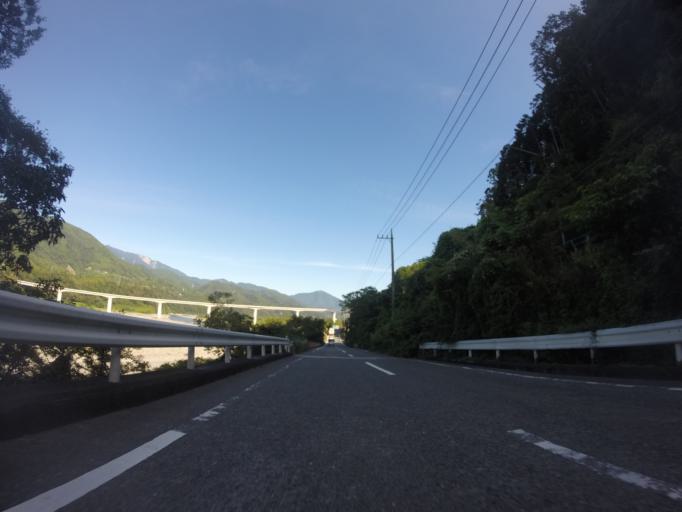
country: JP
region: Shizuoka
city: Fujinomiya
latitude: 35.3073
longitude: 138.4558
